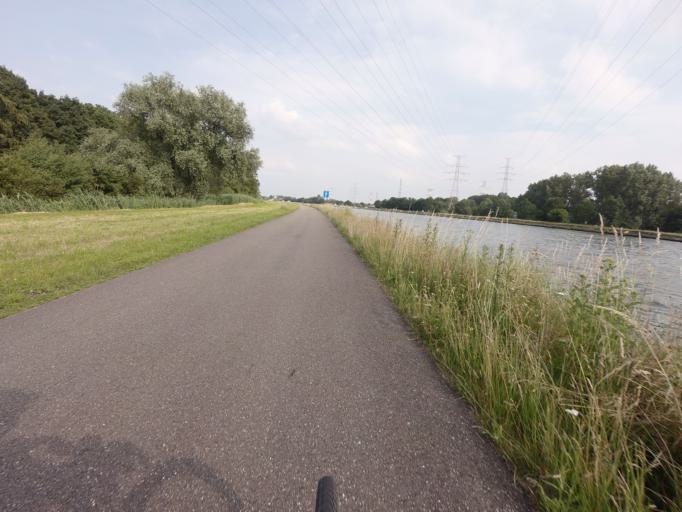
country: BE
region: Flanders
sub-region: Provincie Antwerpen
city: Zandhoven
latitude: 51.2001
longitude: 4.6231
